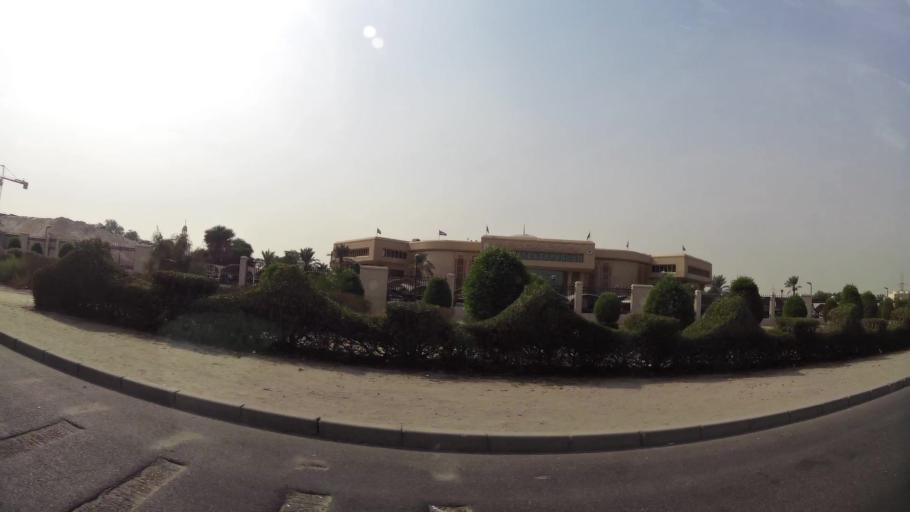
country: KW
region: Al Asimah
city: Ar Rabiyah
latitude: 29.2953
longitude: 47.9465
